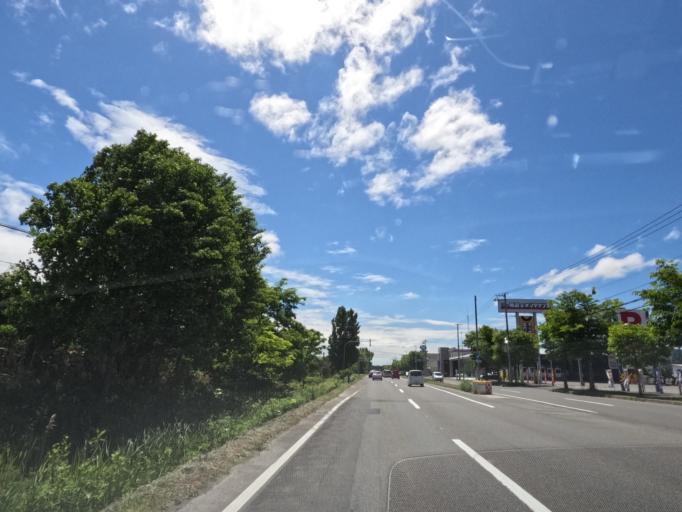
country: JP
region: Hokkaido
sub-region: Asahikawa-shi
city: Asahikawa
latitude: 43.7320
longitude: 142.3649
